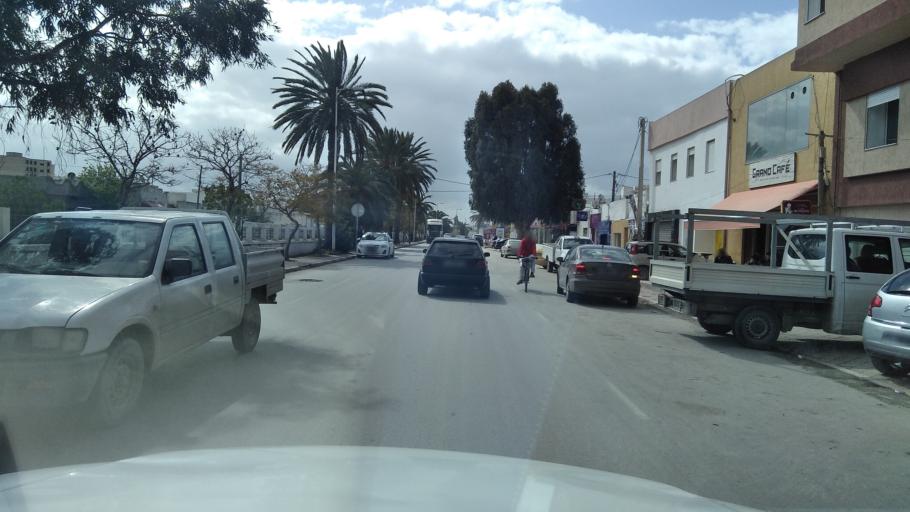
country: TN
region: Bin 'Arus
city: Ben Arous
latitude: 36.7493
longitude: 10.2250
